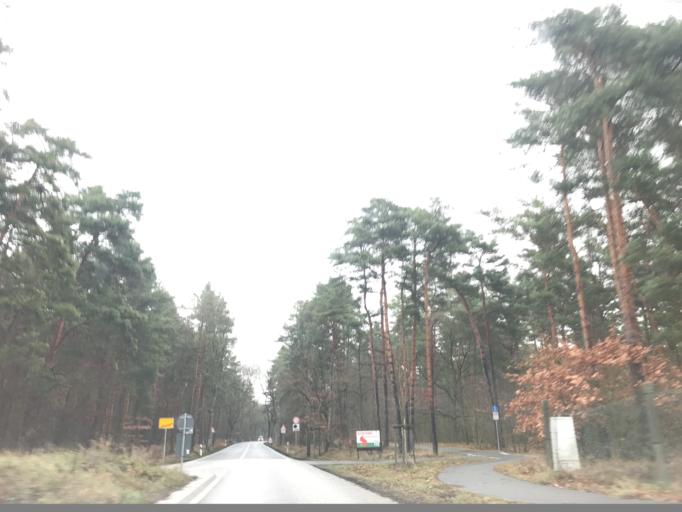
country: DE
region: Brandenburg
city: Nauen
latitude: 52.6911
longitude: 12.9424
